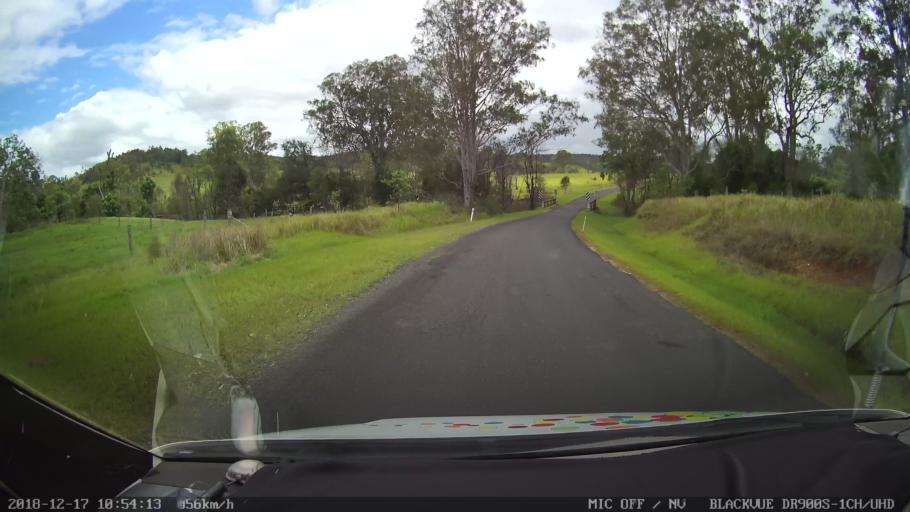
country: AU
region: New South Wales
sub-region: Tenterfield Municipality
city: Carrolls Creek
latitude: -28.8306
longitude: 152.5659
